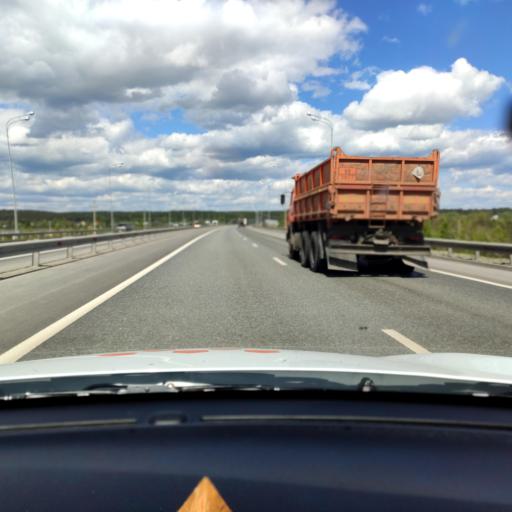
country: RU
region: Tatarstan
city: Osinovo
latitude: 55.8126
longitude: 48.8422
